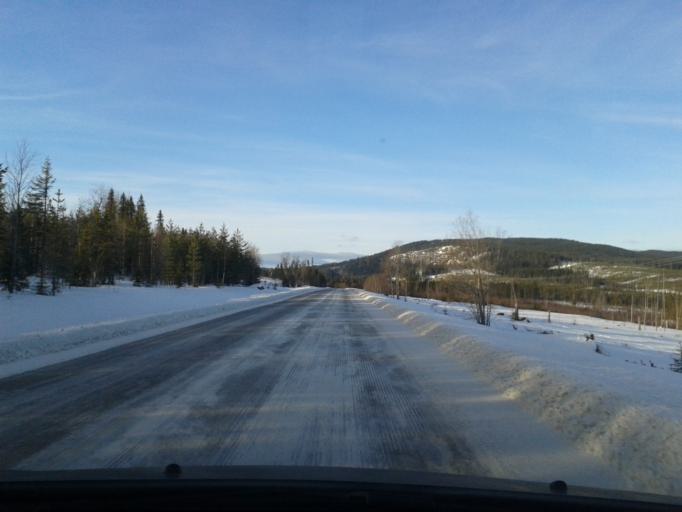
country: SE
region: Vaesterbotten
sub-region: Asele Kommun
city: Asele
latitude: 63.7750
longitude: 17.6739
